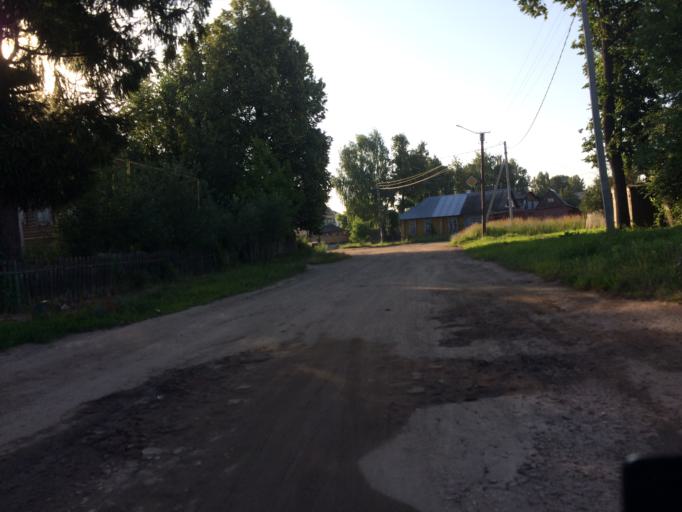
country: RU
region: Mariy-El
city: Yoshkar-Ola
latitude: 56.6508
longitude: 47.9051
